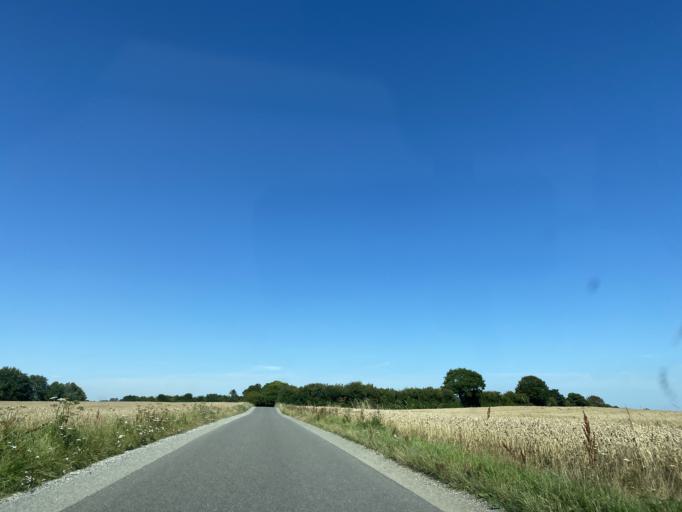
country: DK
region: South Denmark
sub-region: Kolding Kommune
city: Kolding
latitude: 55.5216
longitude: 9.5129
